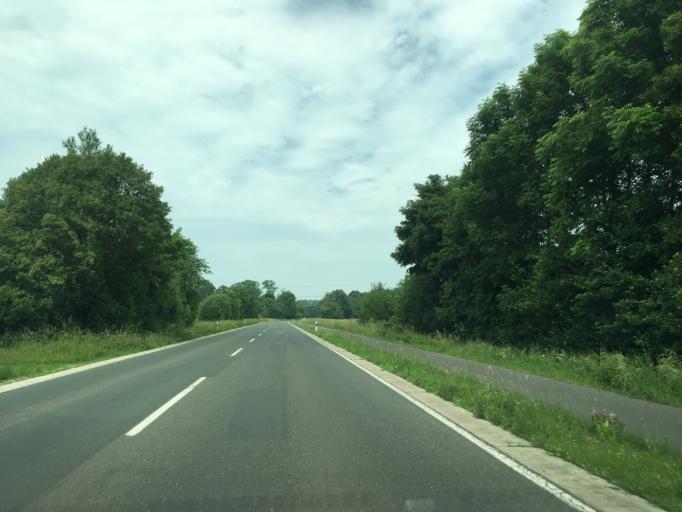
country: DE
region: North Rhine-Westphalia
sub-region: Regierungsbezirk Munster
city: Altenberge
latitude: 52.0749
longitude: 7.4347
